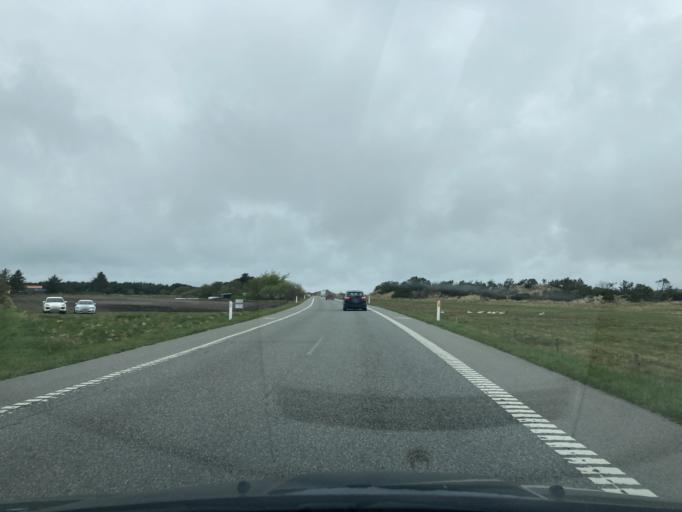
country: DK
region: North Denmark
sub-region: Thisted Kommune
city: Hurup
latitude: 56.9212
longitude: 8.3698
